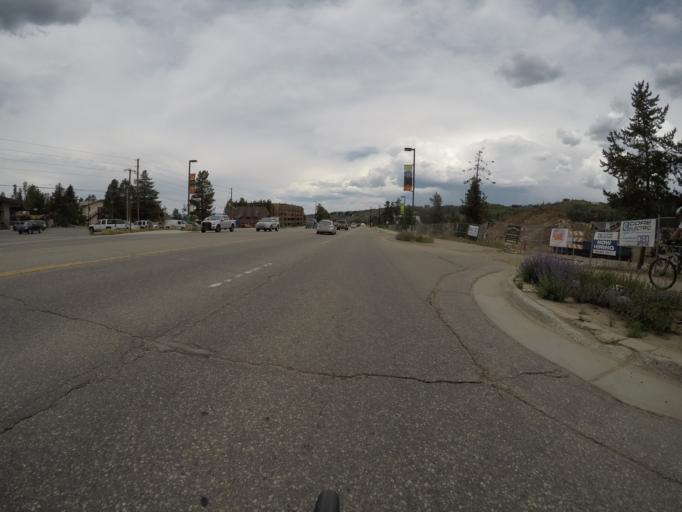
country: US
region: Colorado
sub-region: Grand County
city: Fraser
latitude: 39.9258
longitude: -105.7876
